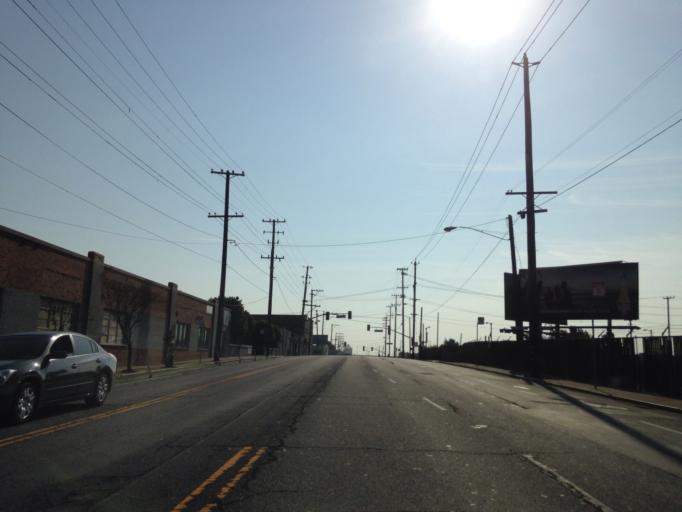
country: US
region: California
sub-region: San Francisco County
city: San Francisco
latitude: 37.7496
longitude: -122.3987
